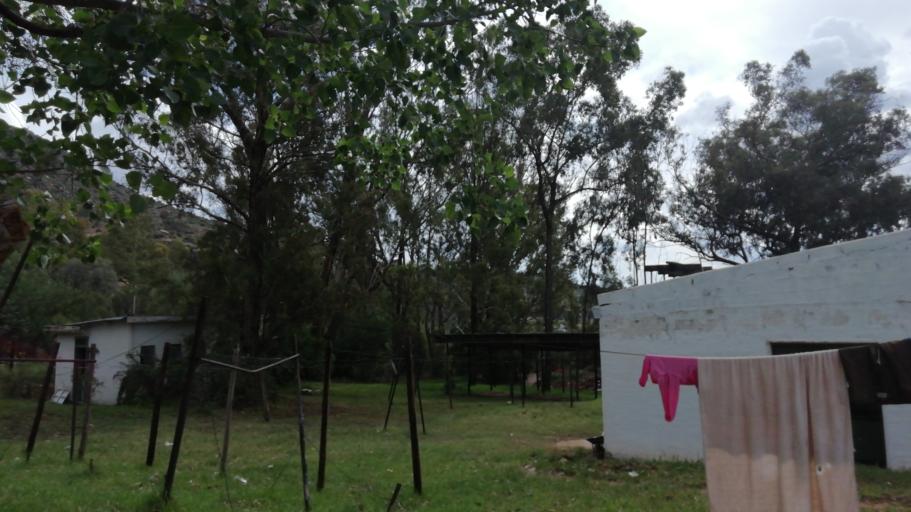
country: LS
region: Maseru
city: Nako
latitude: -29.6316
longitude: 27.5008
